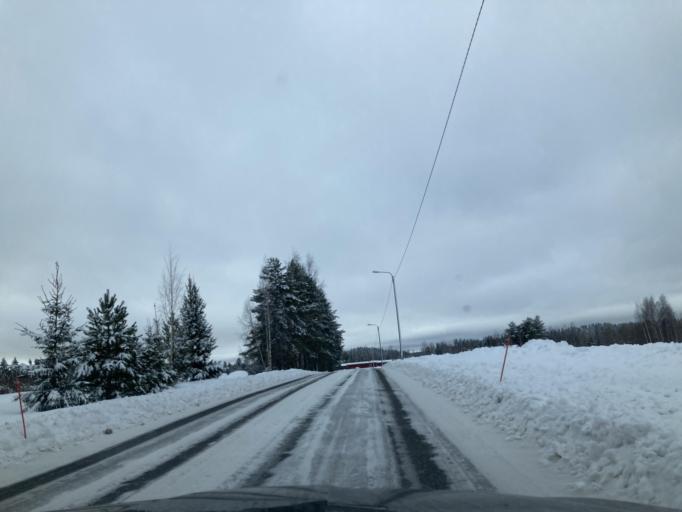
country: FI
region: Central Finland
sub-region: Jaemsae
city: Jaemsae
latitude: 61.8686
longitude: 25.2554
